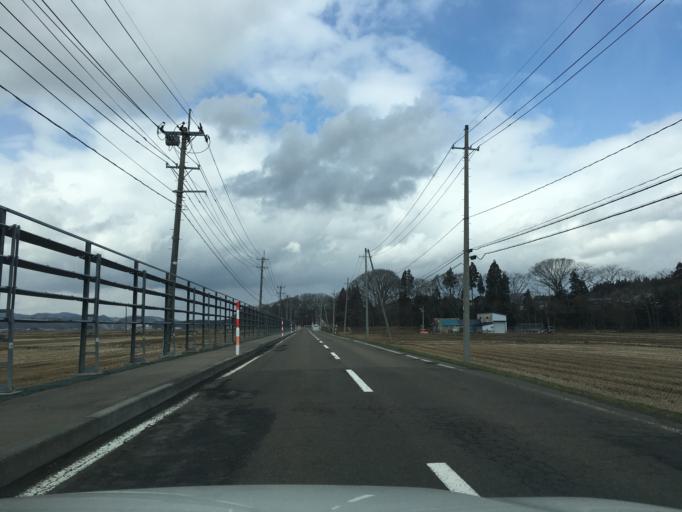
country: JP
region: Akita
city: Takanosu
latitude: 40.1406
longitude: 140.3502
